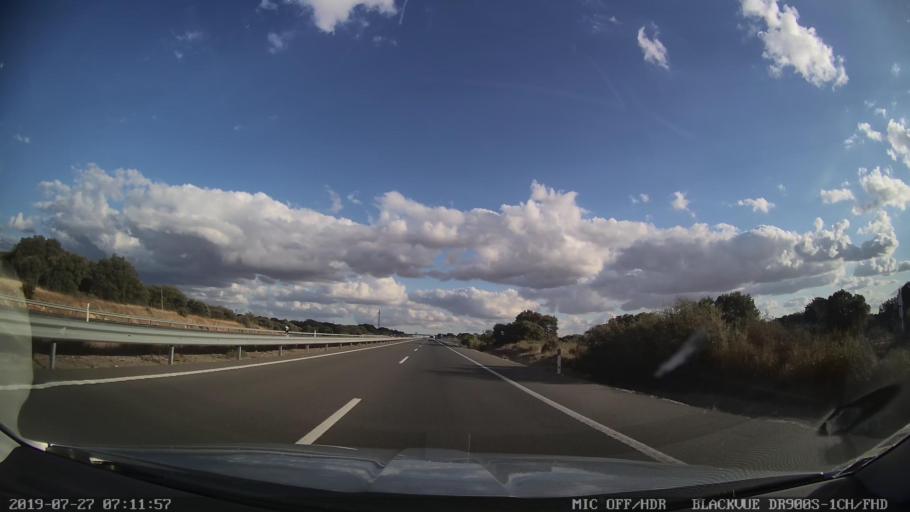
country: ES
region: Extremadura
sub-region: Provincia de Caceres
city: Torrecillas de la Tiesa
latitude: 39.5420
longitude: -5.8336
